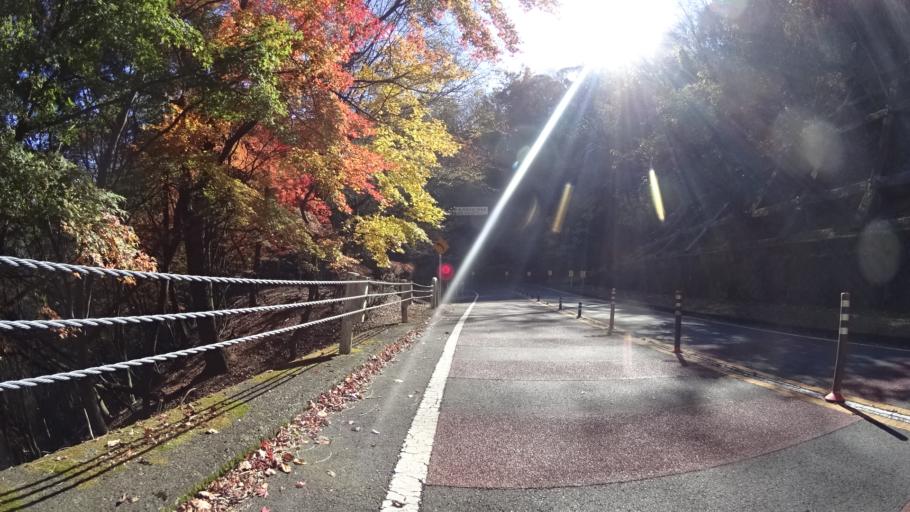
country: JP
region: Yamanashi
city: Uenohara
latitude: 35.7590
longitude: 139.0442
